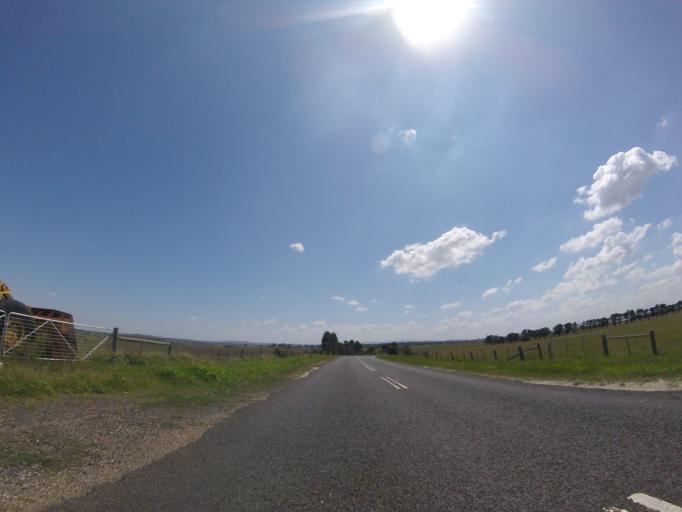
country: AU
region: Victoria
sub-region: Hume
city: Greenvale
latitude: -37.6150
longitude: 144.8136
